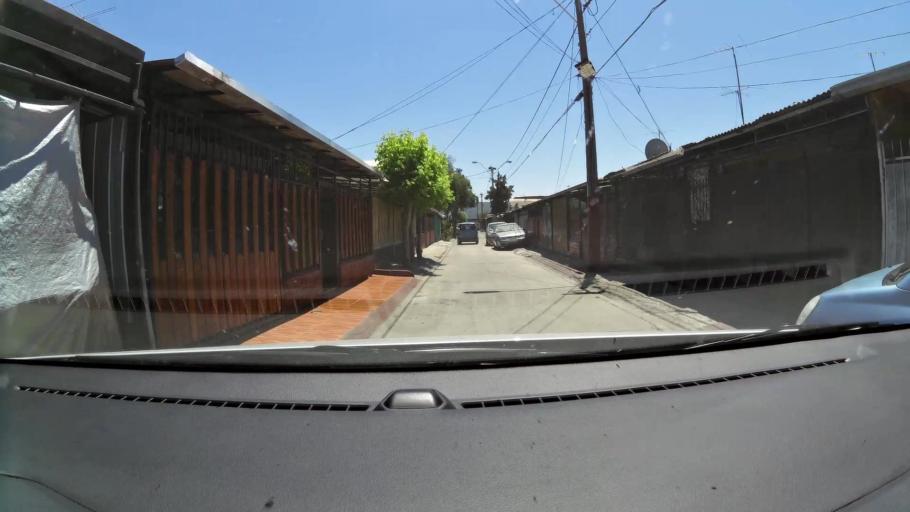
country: CL
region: Santiago Metropolitan
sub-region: Provincia de Santiago
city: La Pintana
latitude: -33.5746
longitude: -70.6658
